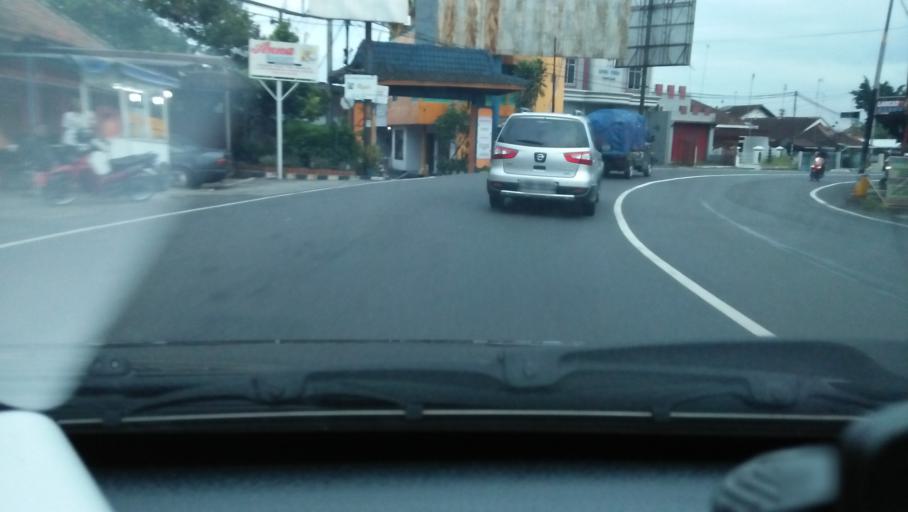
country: ID
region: Central Java
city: Magelang
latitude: -7.4648
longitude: 110.2250
